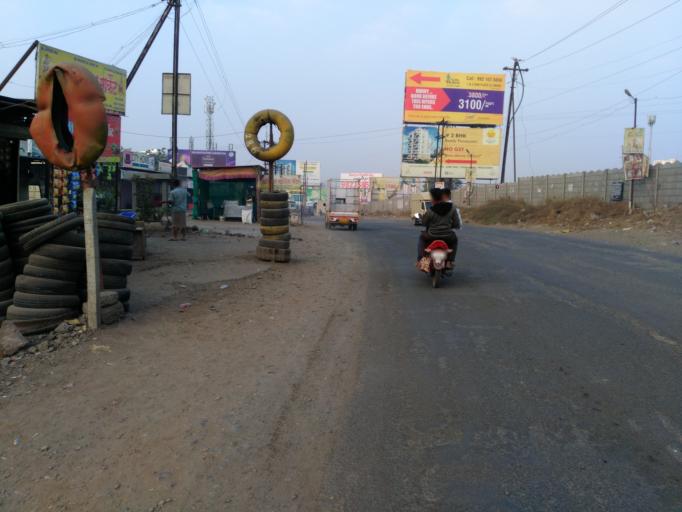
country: IN
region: Maharashtra
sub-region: Pune Division
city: Pune
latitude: 18.4501
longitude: 73.9117
